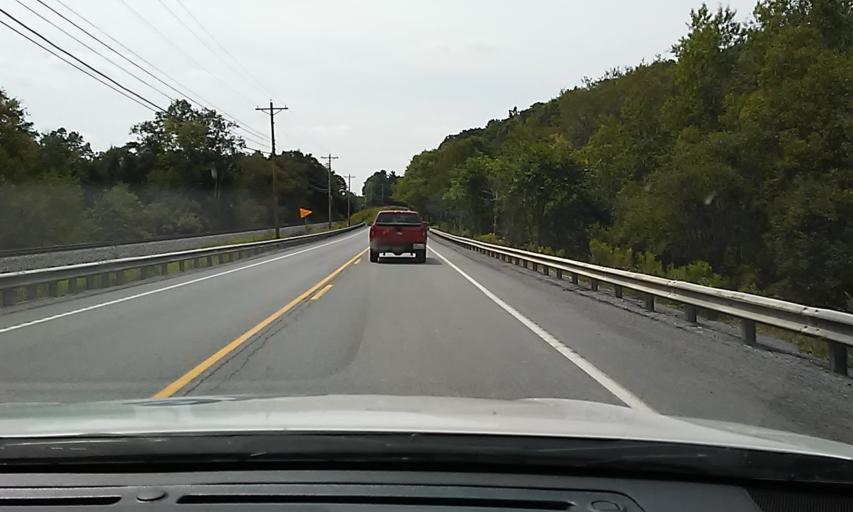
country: US
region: Pennsylvania
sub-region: Clearfield County
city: Treasure Lake
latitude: 41.1471
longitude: -78.6730
